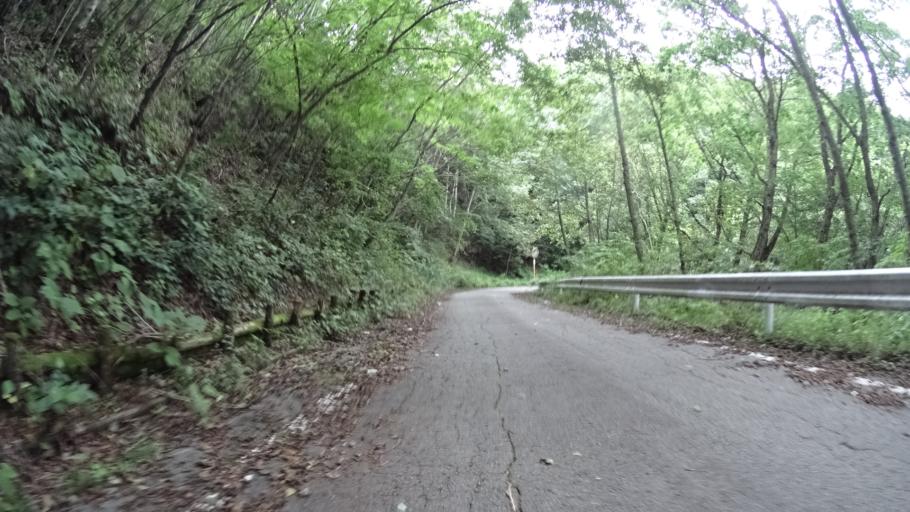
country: JP
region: Yamanashi
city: Nirasaki
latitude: 35.8064
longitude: 138.5461
